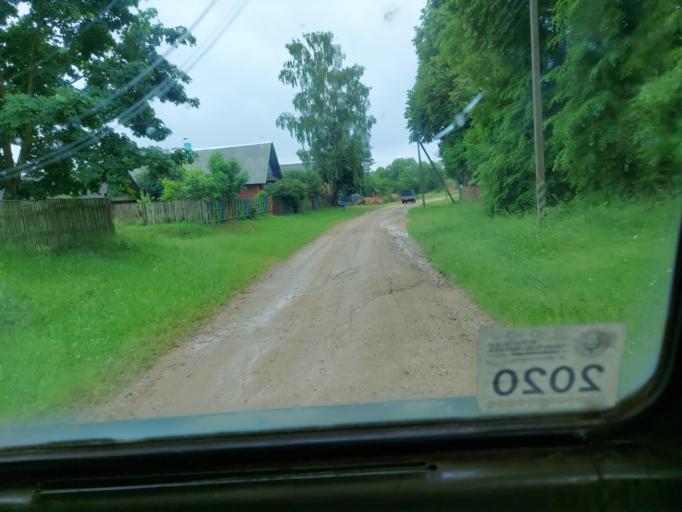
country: BY
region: Mogilev
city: Poselok Voskhod
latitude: 53.6789
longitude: 30.3881
